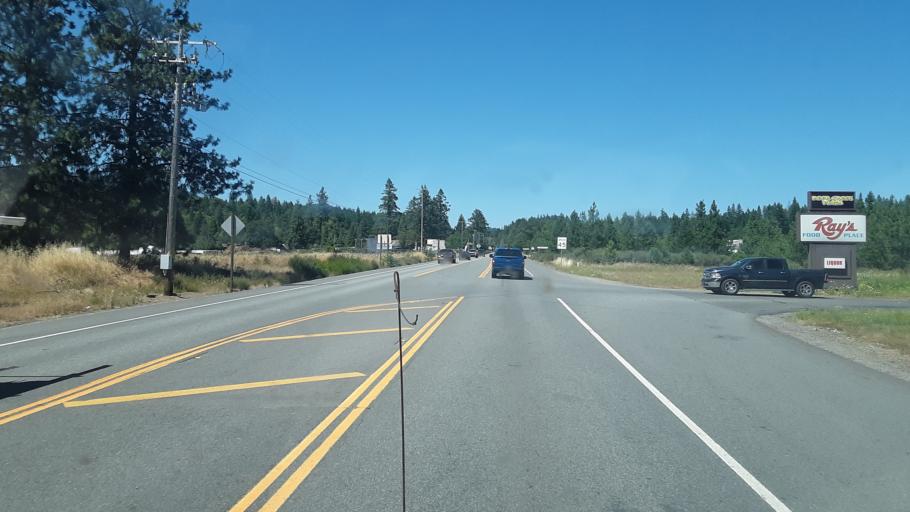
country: US
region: Oregon
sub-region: Josephine County
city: Cave Junction
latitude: 42.2797
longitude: -123.6158
